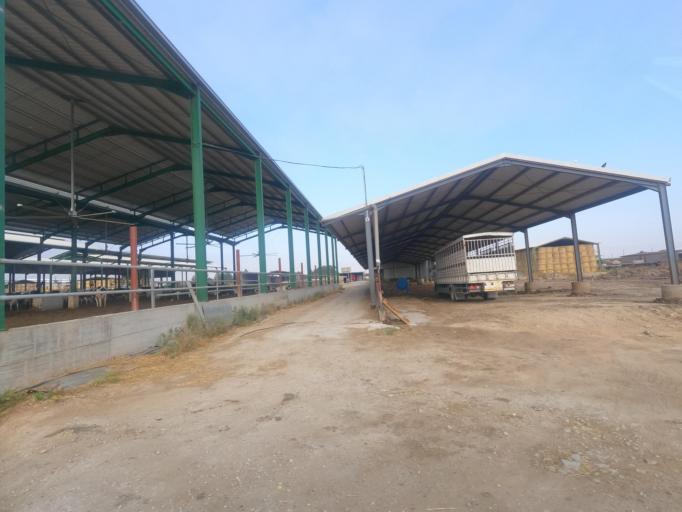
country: CY
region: Ammochostos
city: Achna
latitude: 35.0389
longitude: 33.7869
